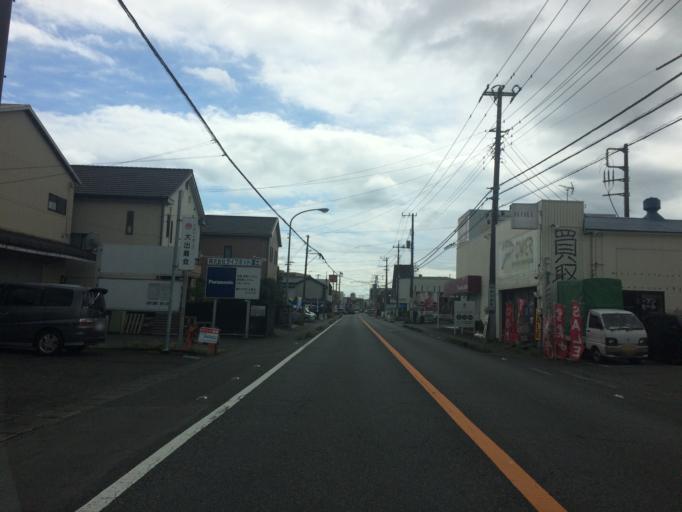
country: JP
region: Shizuoka
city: Fuji
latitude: 35.1640
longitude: 138.6495
